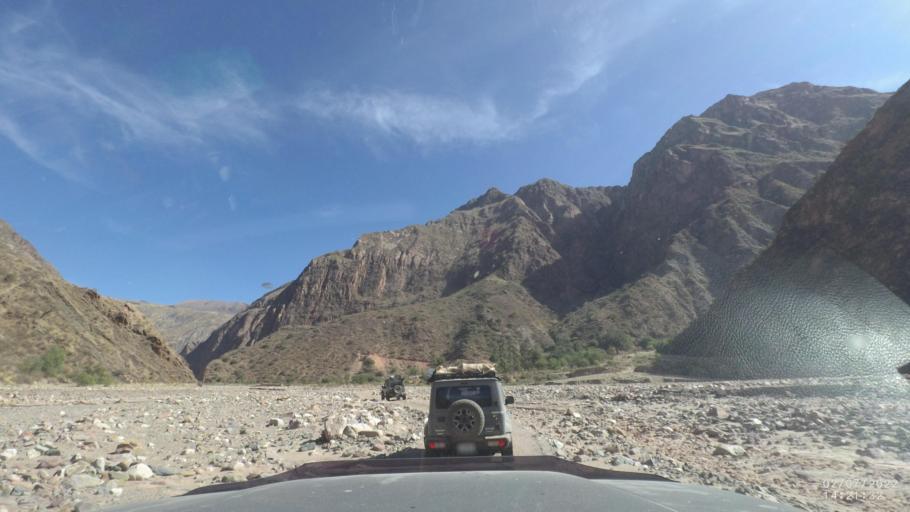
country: BO
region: Cochabamba
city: Irpa Irpa
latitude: -17.8290
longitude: -66.4124
